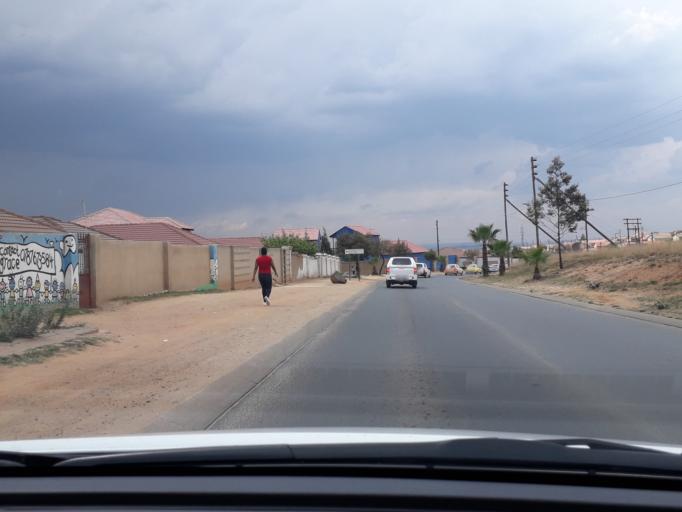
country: ZA
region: Gauteng
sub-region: West Rand District Municipality
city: Muldersdriseloop
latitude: -26.0436
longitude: 27.9221
